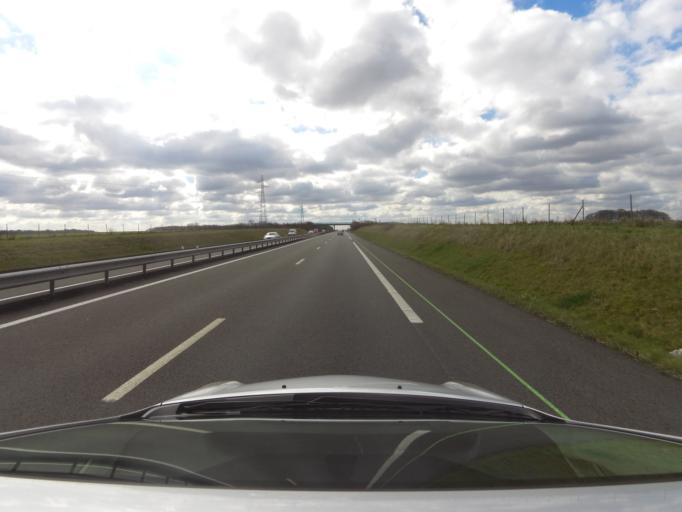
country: FR
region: Picardie
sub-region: Departement de la Somme
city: Rue
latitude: 50.2987
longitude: 1.7274
